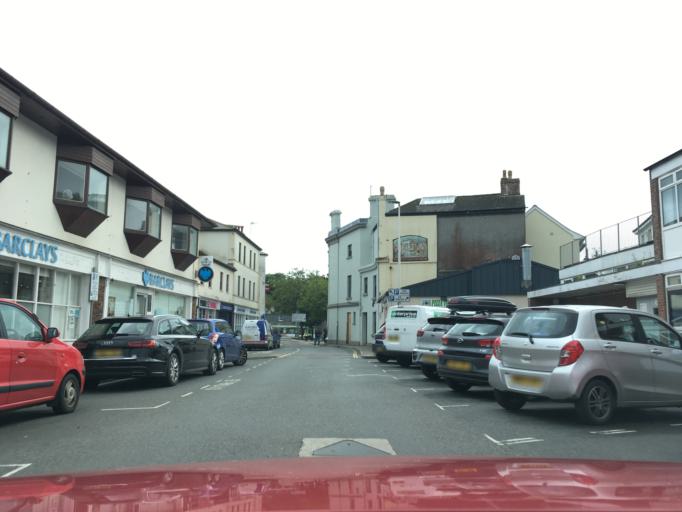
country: GB
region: England
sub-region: Devon
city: Kingsbridge
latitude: 50.2842
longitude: -3.7764
